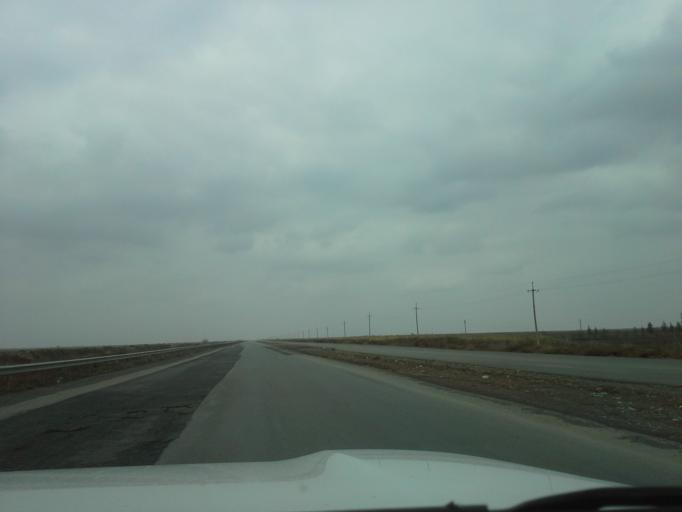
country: TM
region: Ahal
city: Tejen
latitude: 37.3041
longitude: 60.7814
